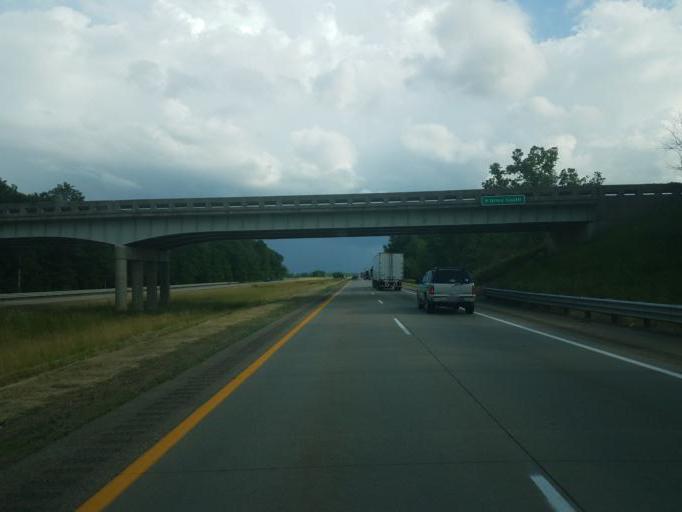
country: US
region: Michigan
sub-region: Calhoun County
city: Marshall
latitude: 42.1317
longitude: -84.9956
